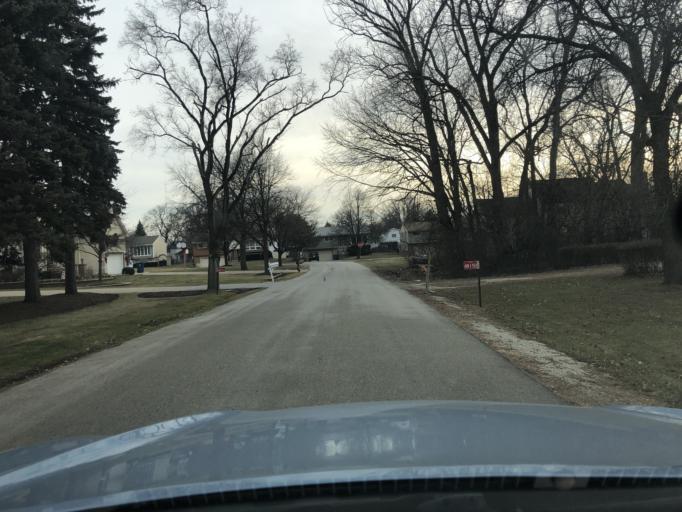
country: US
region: Illinois
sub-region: DuPage County
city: Addison
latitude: 41.9372
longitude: -88.0105
